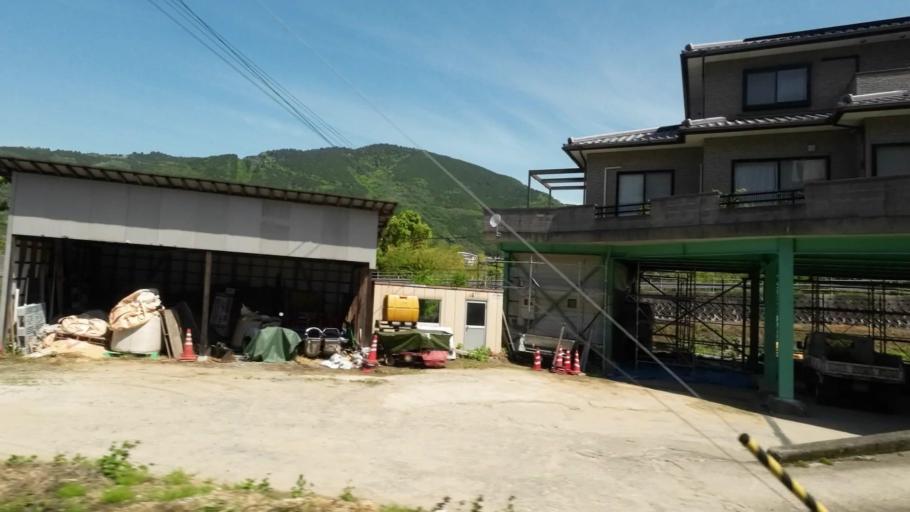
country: JP
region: Tokushima
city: Ikedacho
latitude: 34.0323
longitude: 133.8505
